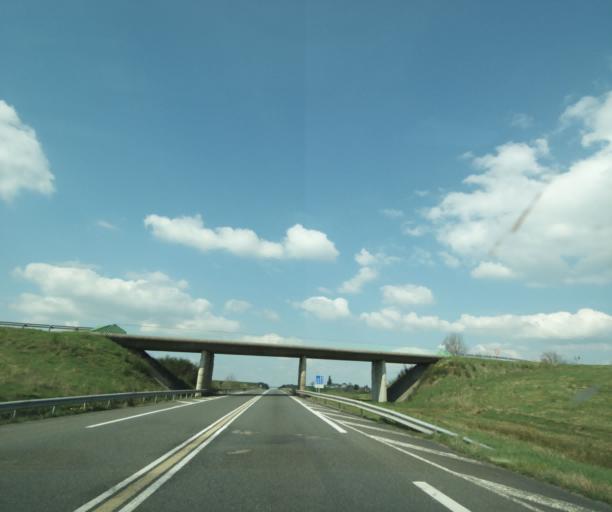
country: FR
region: Auvergne
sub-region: Departement de l'Allier
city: Montmarault
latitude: 46.3756
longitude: 3.0291
